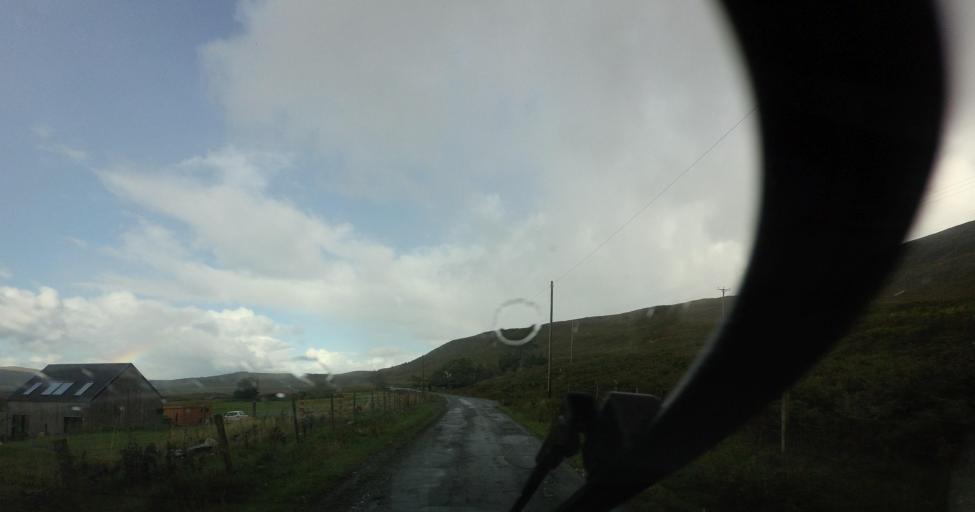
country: GB
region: Scotland
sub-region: Highland
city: Portree
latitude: 57.2187
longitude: -5.9388
